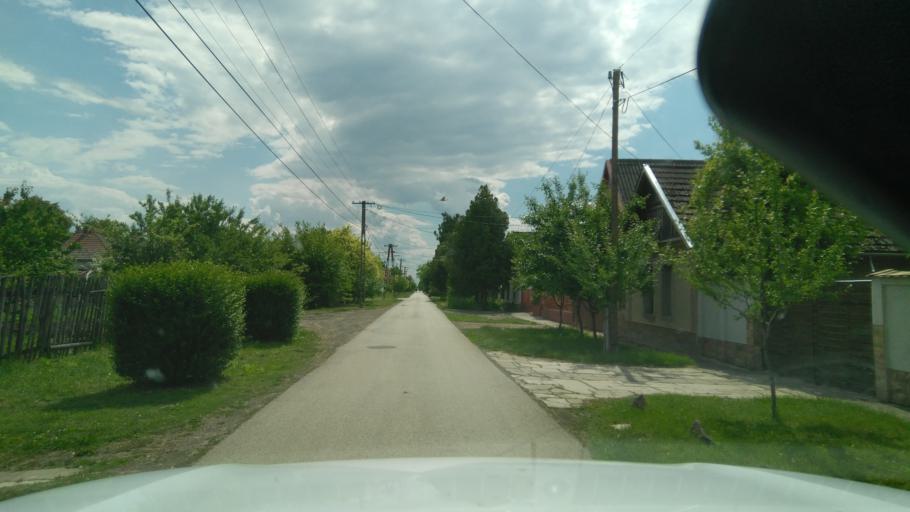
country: HU
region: Bekes
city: Magyarbanhegyes
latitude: 46.4596
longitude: 20.9568
